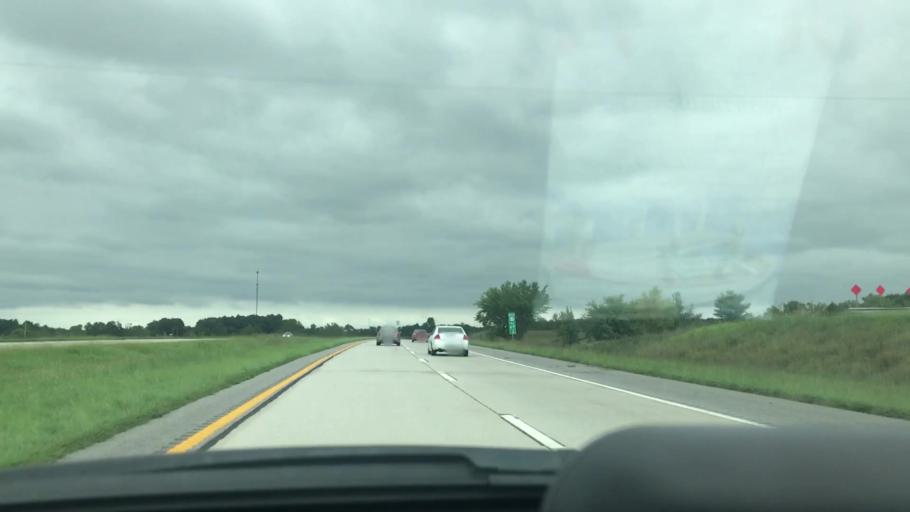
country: US
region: Missouri
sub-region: Greene County
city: Fair Grove
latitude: 37.4453
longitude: -93.1439
